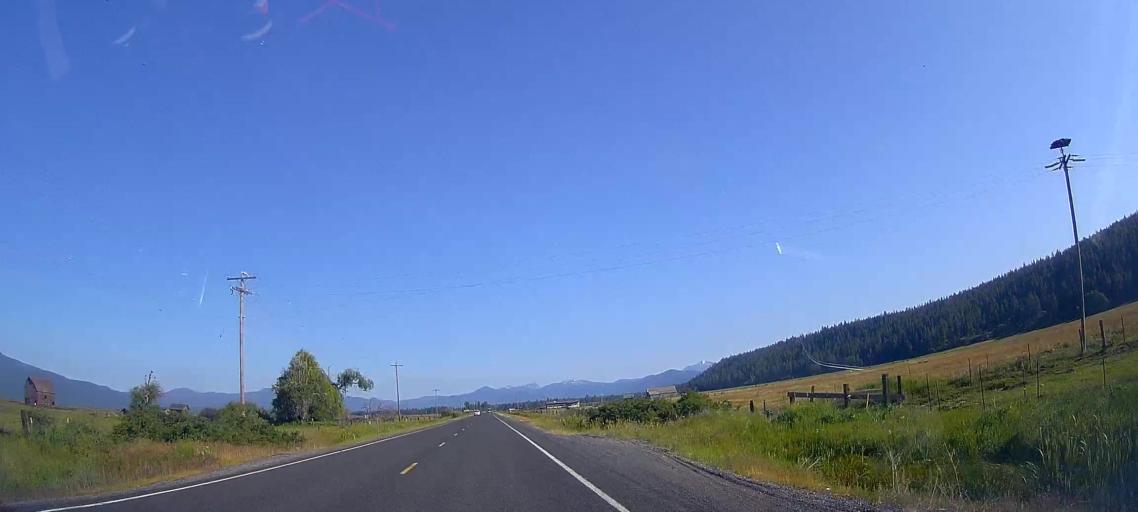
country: US
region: Oregon
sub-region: Klamath County
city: Klamath Falls
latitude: 42.6499
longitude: -121.9556
